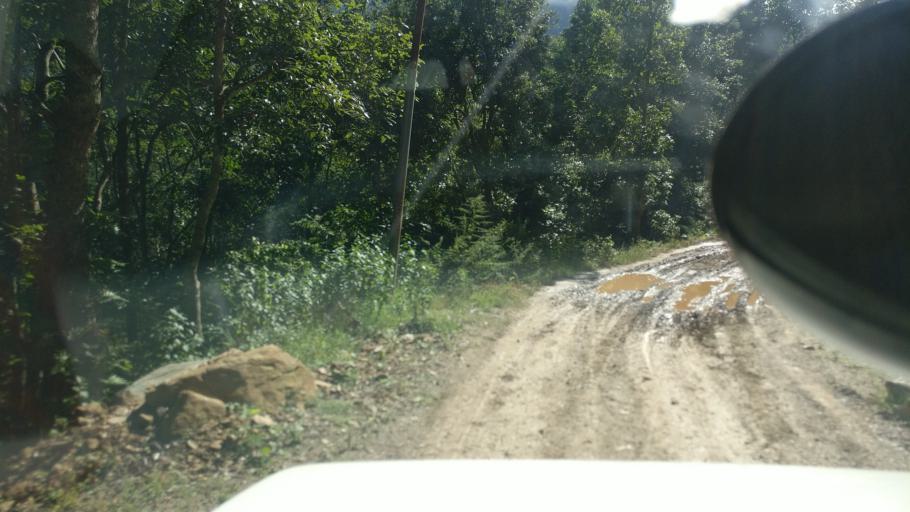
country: NP
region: Western Region
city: Baglung
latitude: 28.1241
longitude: 83.6701
